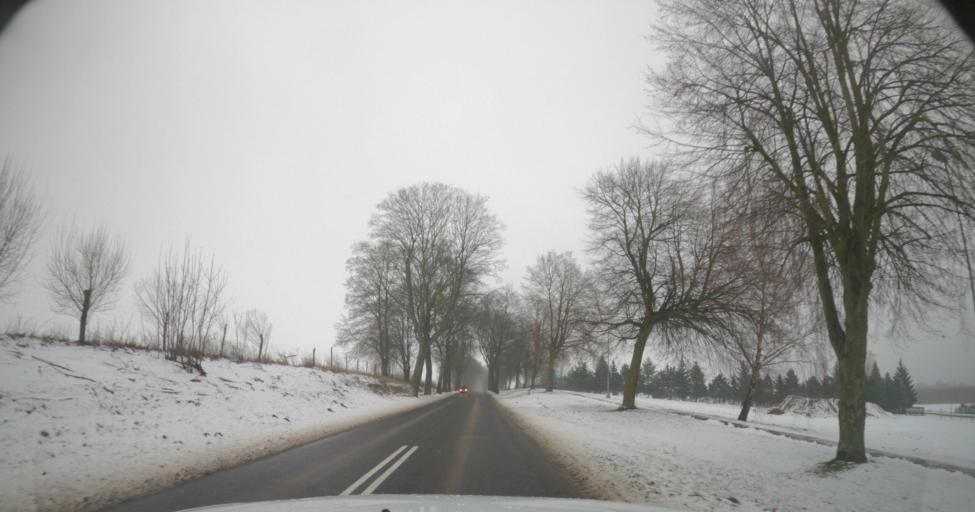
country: PL
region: West Pomeranian Voivodeship
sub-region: Powiat gryficki
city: Gryfice
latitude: 53.9109
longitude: 15.2249
